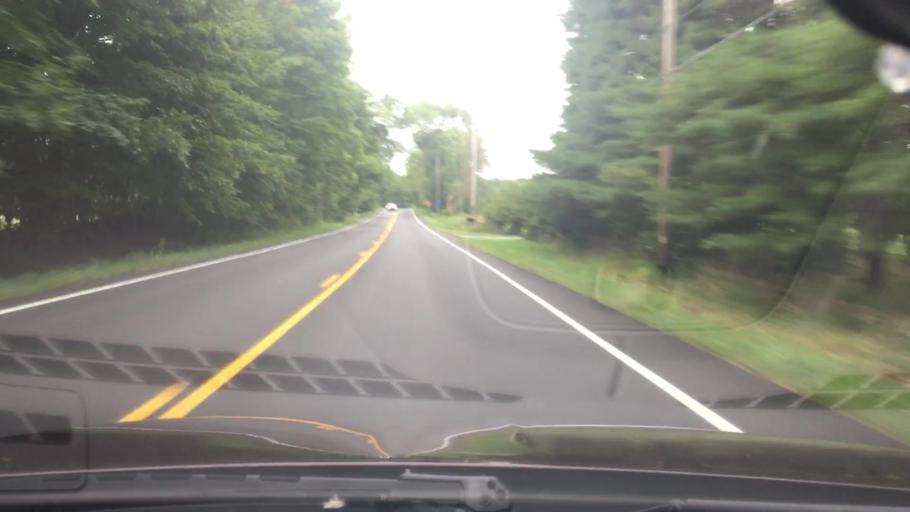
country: US
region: New York
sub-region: Dutchess County
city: Millbrook
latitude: 41.8322
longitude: -73.6165
